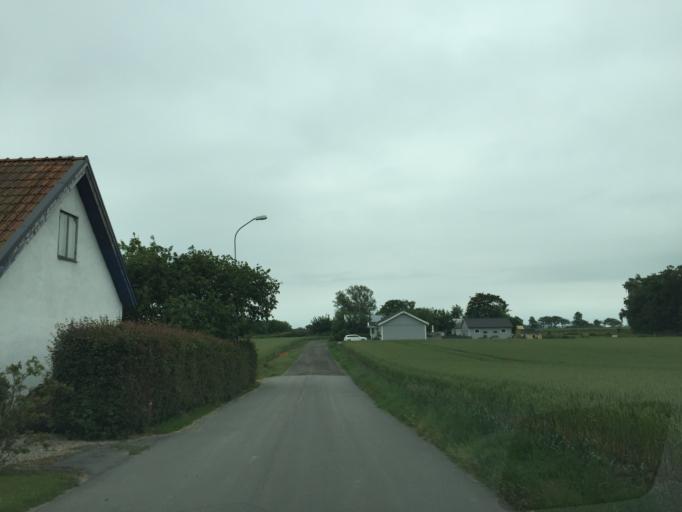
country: SE
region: Skane
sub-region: Ystads Kommun
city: Kopingebro
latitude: 55.4380
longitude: 14.1055
